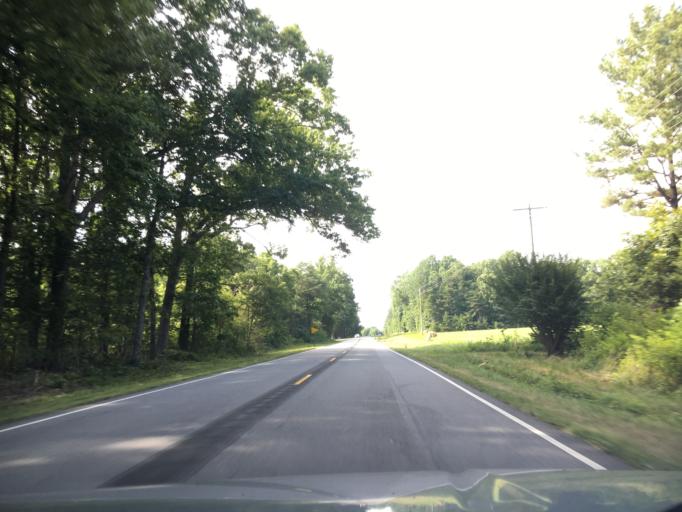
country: US
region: Virginia
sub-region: Halifax County
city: Mountain Road
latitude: 36.8965
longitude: -79.0173
